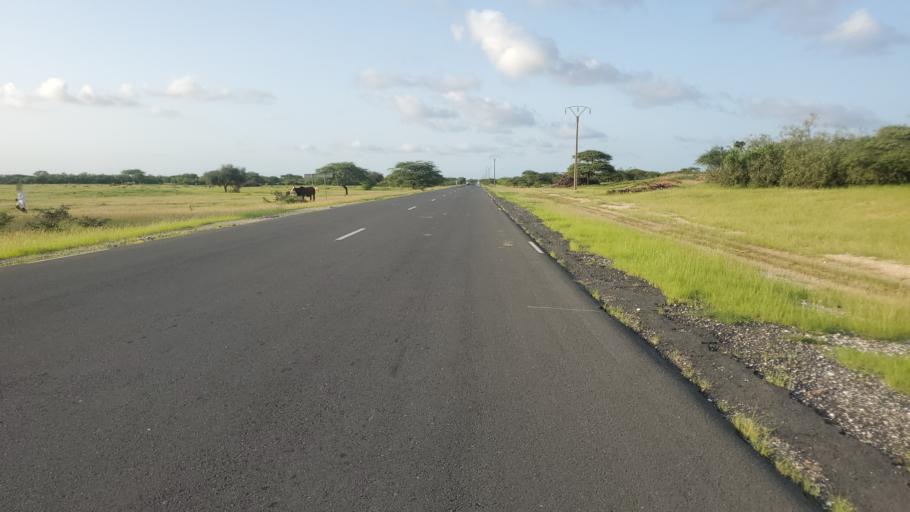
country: SN
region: Saint-Louis
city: Saint-Louis
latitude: 16.1597
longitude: -16.4101
